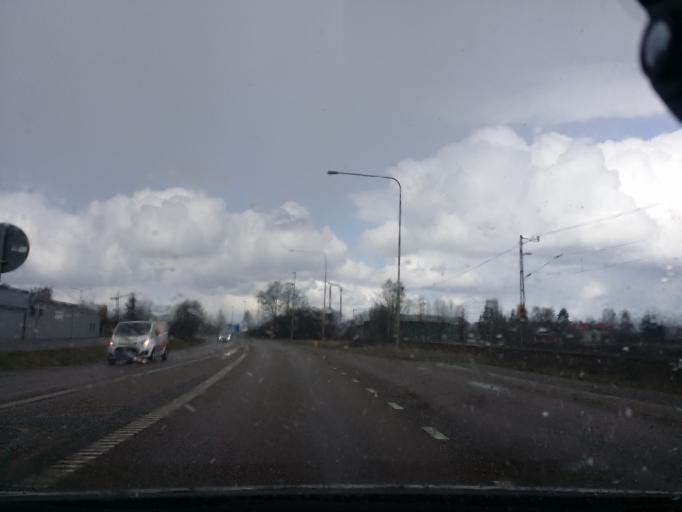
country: SE
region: Vaestmanland
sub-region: Sala Kommun
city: Sala
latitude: 59.9119
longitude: 16.6193
